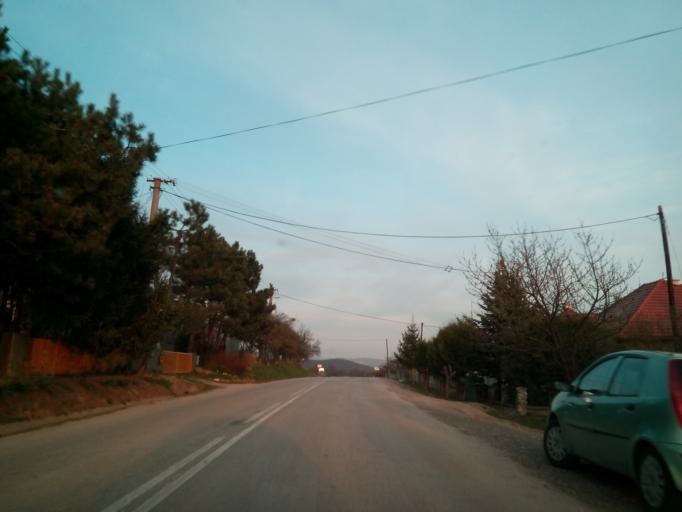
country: SK
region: Kosicky
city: Roznava
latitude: 48.6605
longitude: 20.4650
